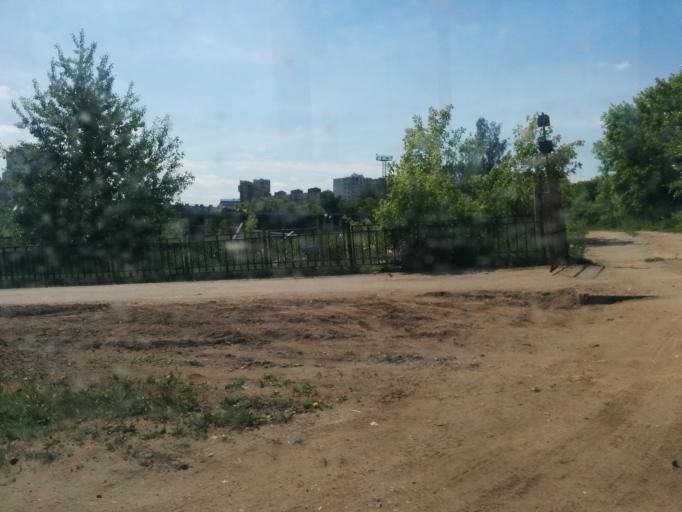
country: RU
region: Perm
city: Perm
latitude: 58.0085
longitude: 56.2962
